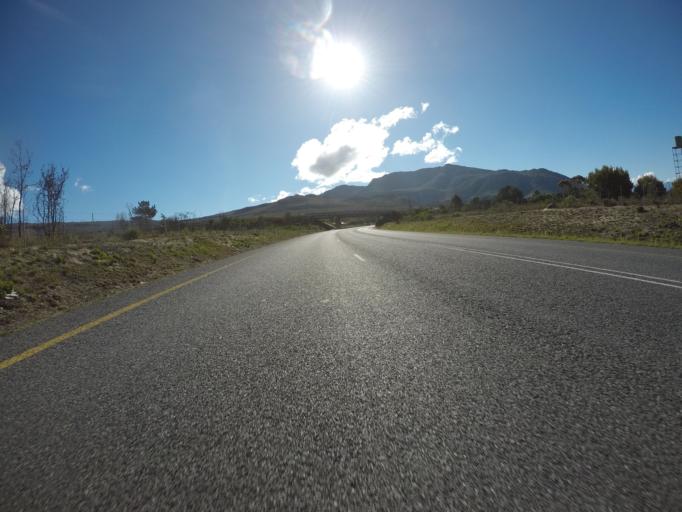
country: ZA
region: Western Cape
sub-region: Overberg District Municipality
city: Grabouw
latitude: -34.2318
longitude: 19.1883
